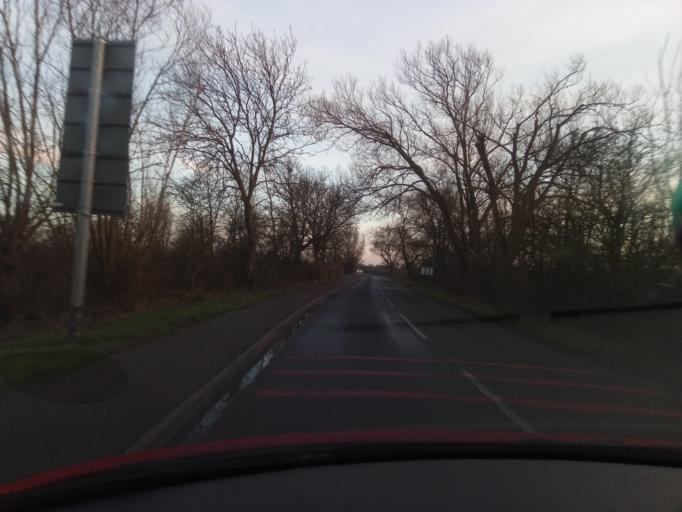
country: GB
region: England
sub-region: Leicestershire
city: Sileby
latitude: 52.7331
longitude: -1.1290
